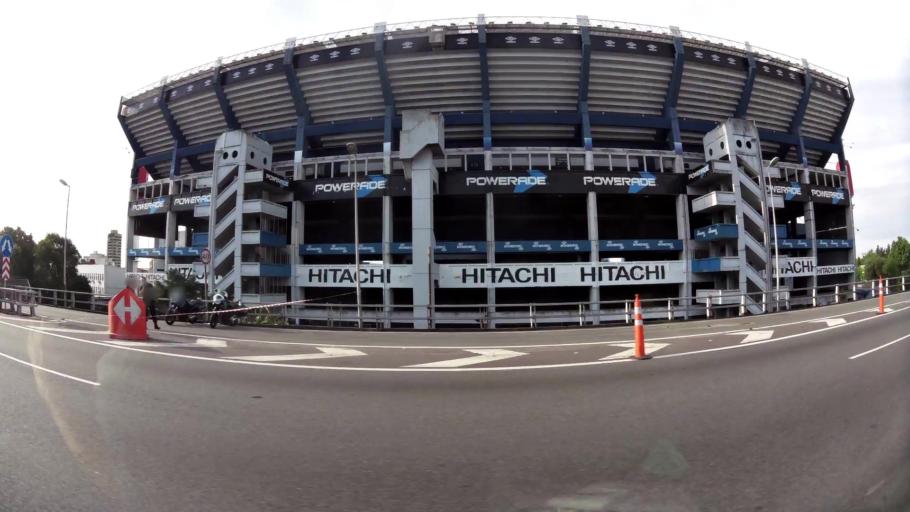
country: AR
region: Buenos Aires F.D.
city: Villa Santa Rita
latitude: -34.6367
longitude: -58.5199
